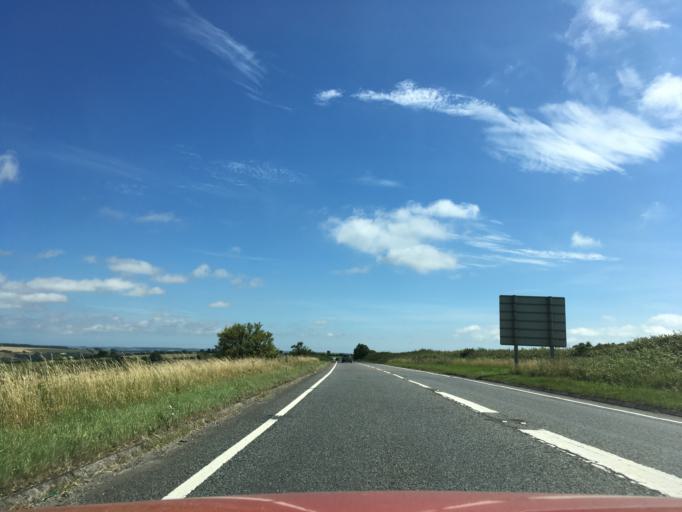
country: GB
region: England
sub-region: Dorset
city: Dorchester
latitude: 50.7963
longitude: -2.5488
